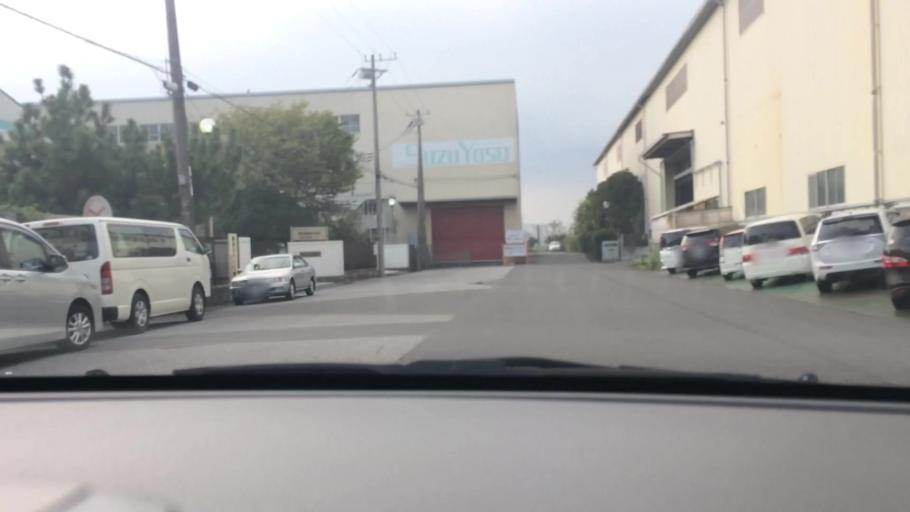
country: JP
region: Tokyo
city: Urayasu
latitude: 35.6292
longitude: 139.9074
